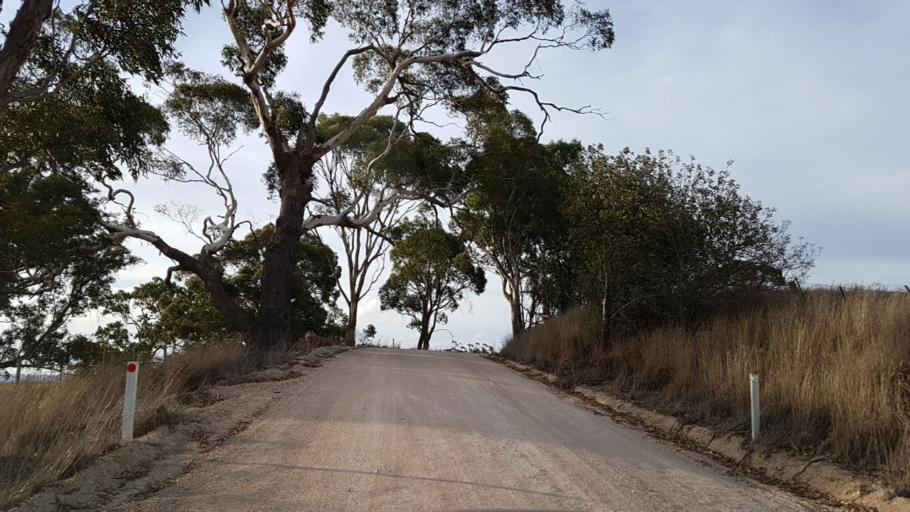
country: AU
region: South Australia
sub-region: Mount Barker
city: Nairne
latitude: -35.0144
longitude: 138.9103
